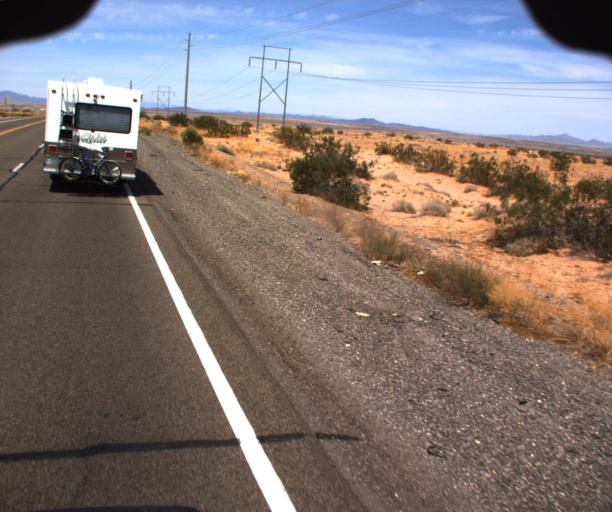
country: US
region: Arizona
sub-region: La Paz County
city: Parker
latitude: 33.9553
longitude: -114.2169
